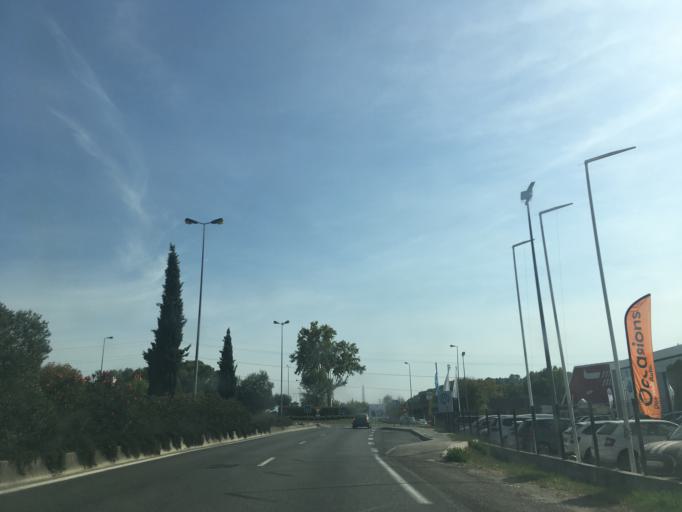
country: FR
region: Provence-Alpes-Cote d'Azur
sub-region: Departement du Var
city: Trans-en-Provence
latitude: 43.5153
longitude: 6.4759
